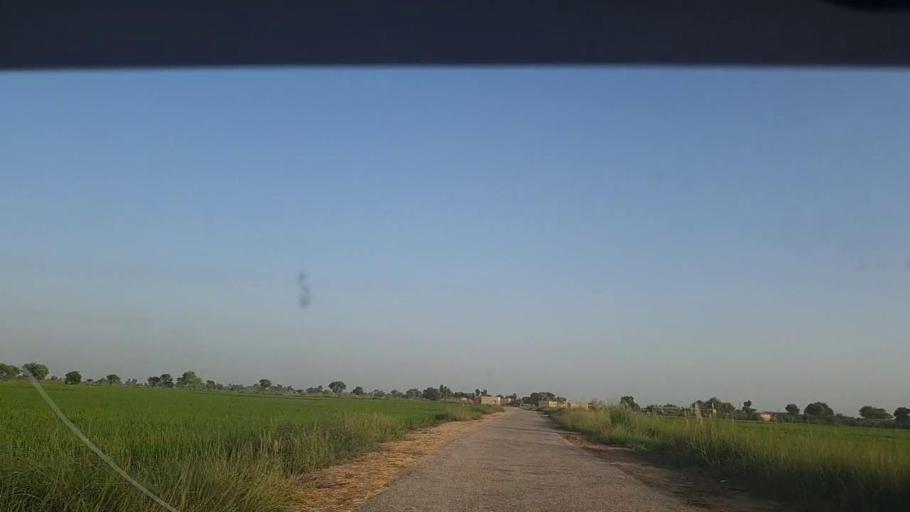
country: PK
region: Sindh
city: Thul
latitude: 28.1332
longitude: 68.8901
